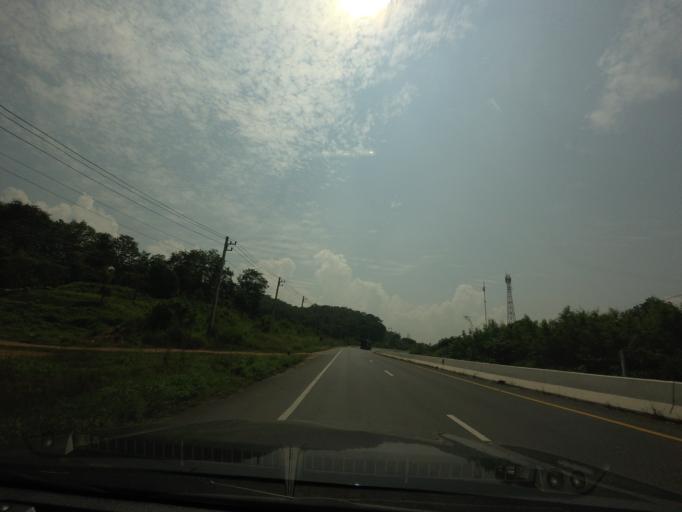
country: TH
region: Phrae
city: Den Chai
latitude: 17.9376
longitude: 100.0611
